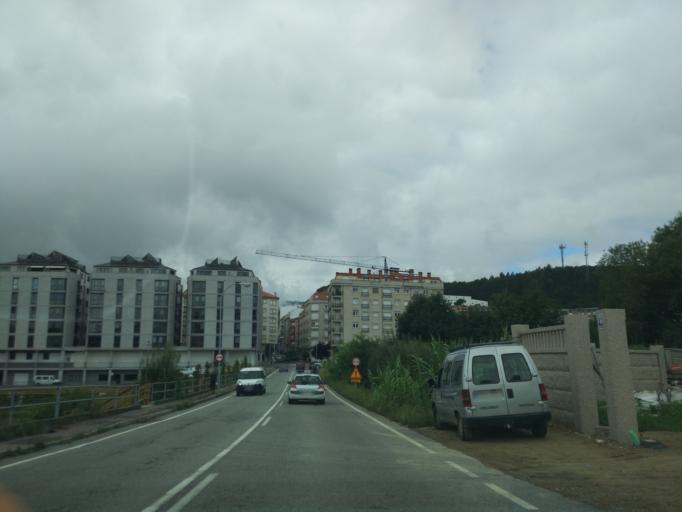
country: ES
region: Galicia
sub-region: Provincia da Coruna
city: Boiro
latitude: 42.6474
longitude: -8.8769
